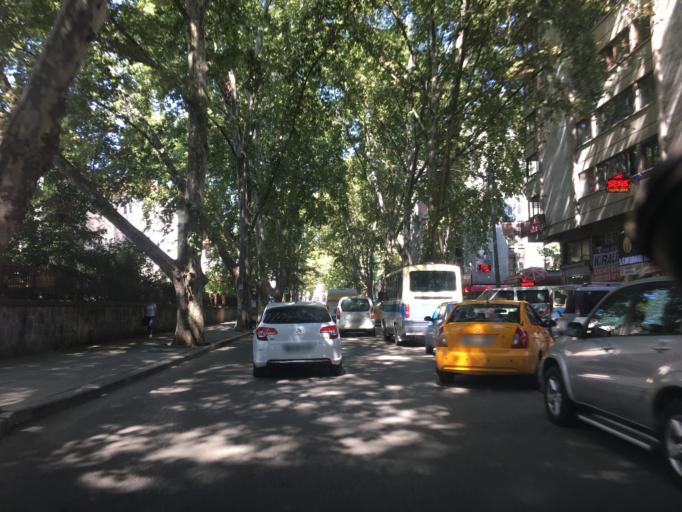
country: TR
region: Ankara
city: Ankara
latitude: 39.9201
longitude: 32.8504
